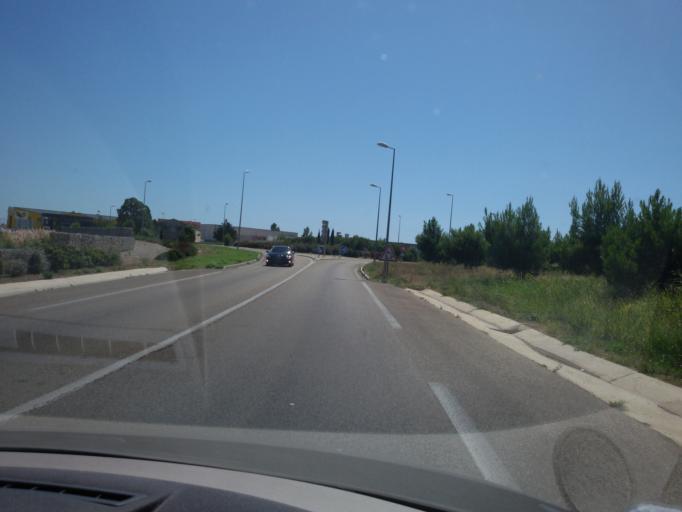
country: FR
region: Languedoc-Roussillon
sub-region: Departement de l'Herault
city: Frontignan
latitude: 43.4670
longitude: 3.7663
